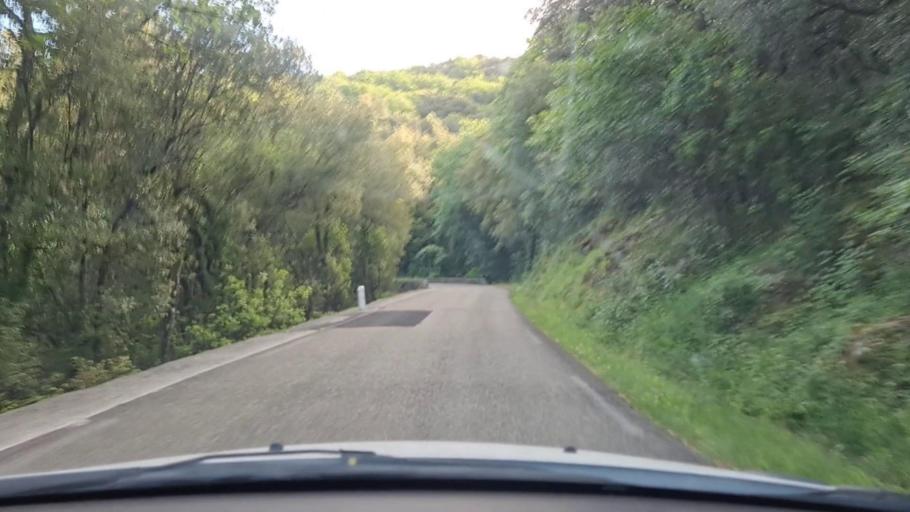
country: FR
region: Languedoc-Roussillon
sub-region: Departement du Gard
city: Les Salles-du-Gardon
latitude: 44.1717
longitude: 4.0240
